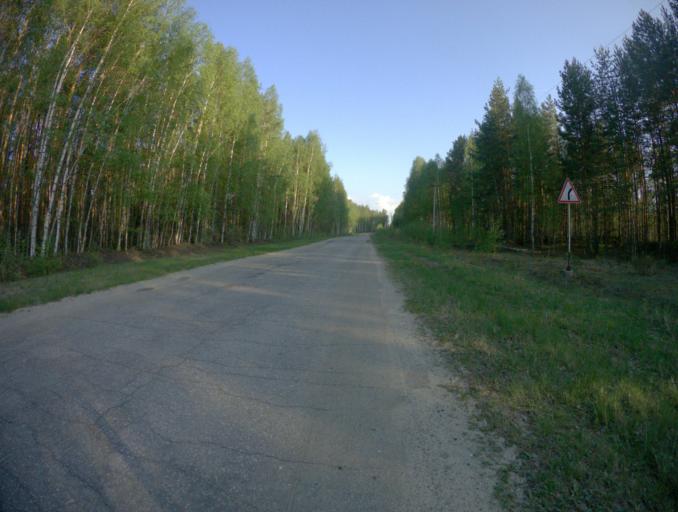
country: RU
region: Vladimir
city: Vyazniki
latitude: 56.3460
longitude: 42.1386
